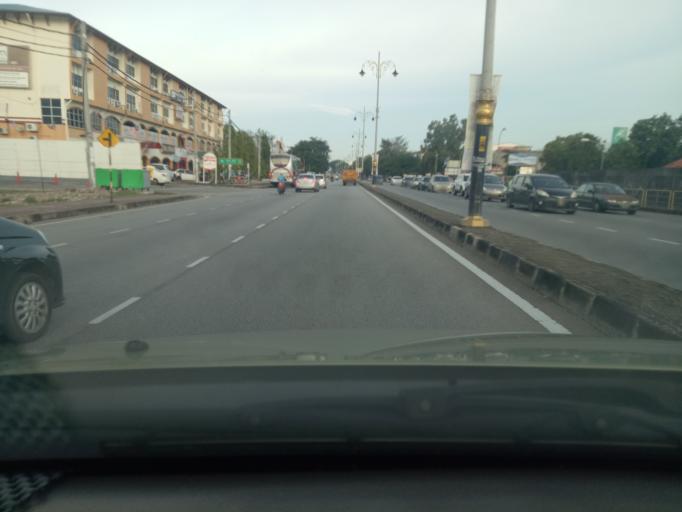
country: MY
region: Kedah
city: Alor Setar
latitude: 6.1270
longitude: 100.3533
